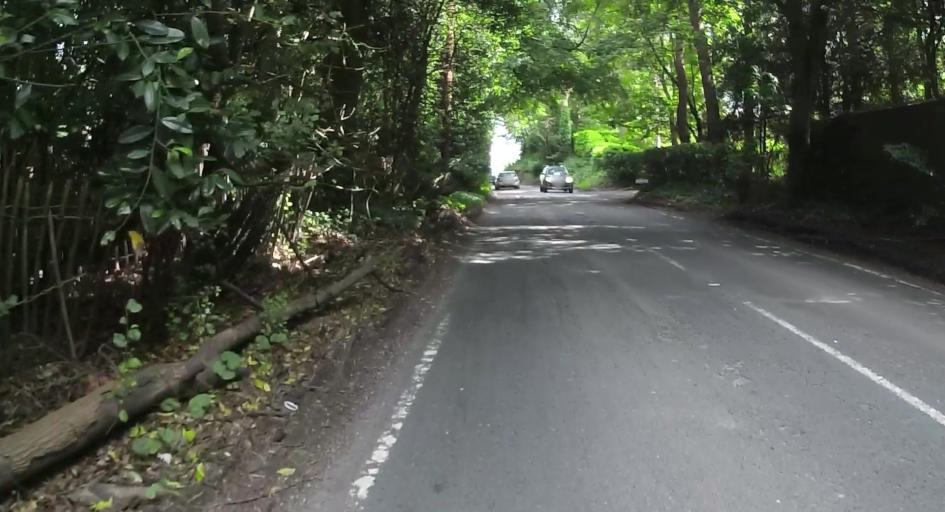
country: GB
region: England
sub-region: Wokingham
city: Finchampstead
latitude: 51.3668
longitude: -0.8546
